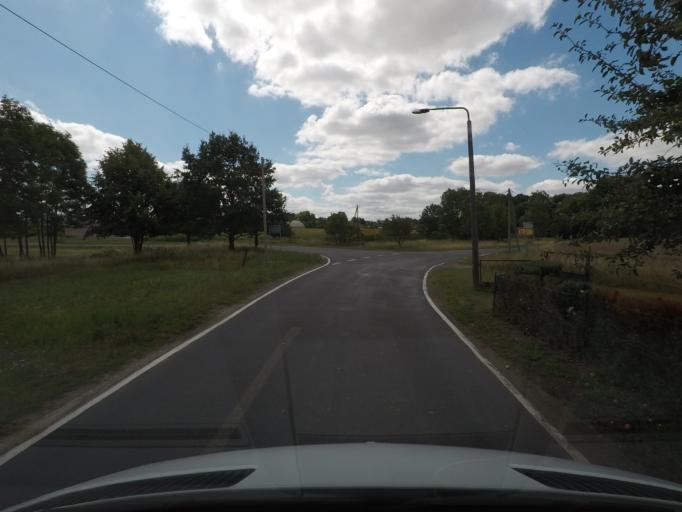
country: DE
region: Brandenburg
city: Brussow
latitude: 53.3579
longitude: 14.1495
